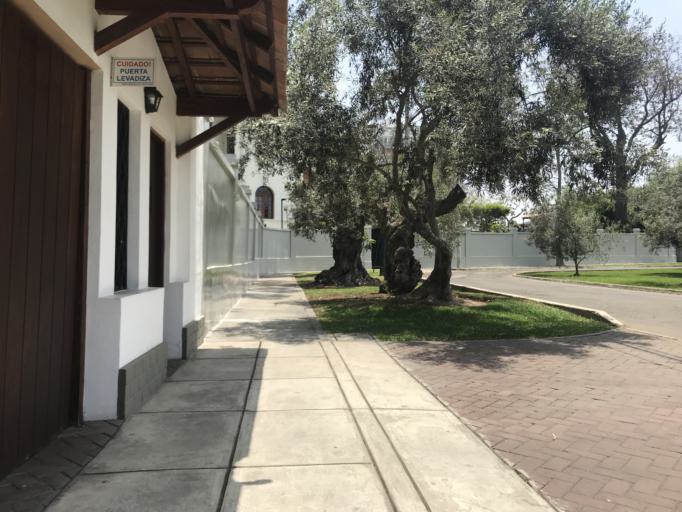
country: PE
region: Lima
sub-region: Lima
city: San Isidro
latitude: -12.0976
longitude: -77.0336
